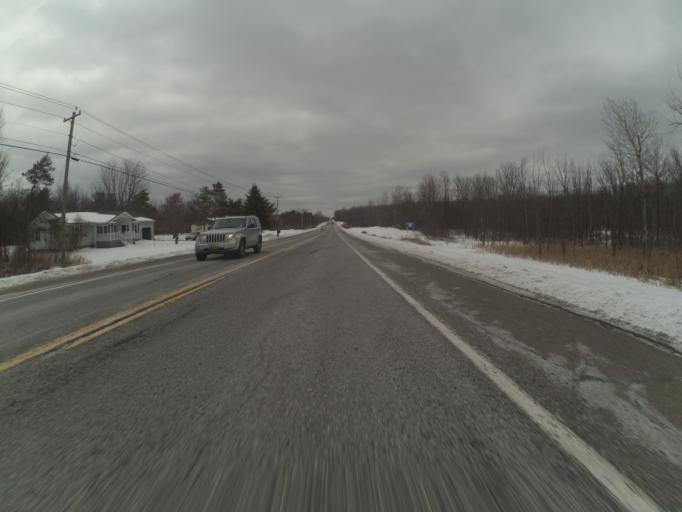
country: US
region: New York
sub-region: St. Lawrence County
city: Potsdam
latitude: 44.7044
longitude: -74.9337
